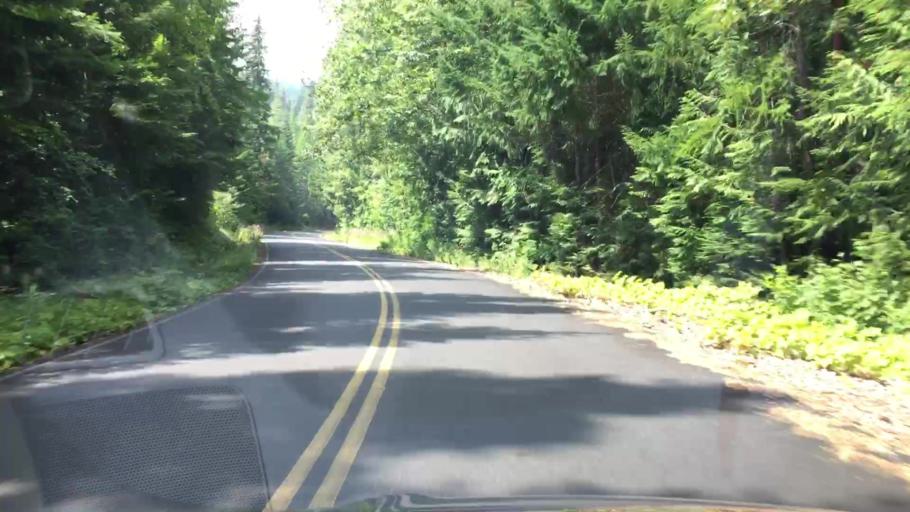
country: US
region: Washington
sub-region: Klickitat County
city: White Salmon
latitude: 46.0817
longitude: -121.5931
